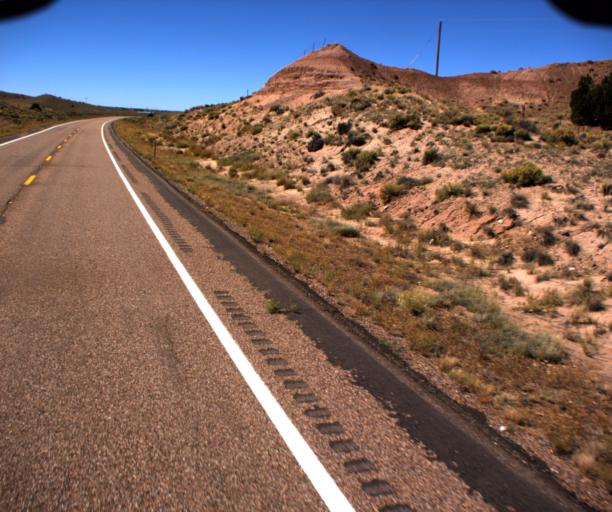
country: US
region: Arizona
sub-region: Apache County
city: Saint Johns
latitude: 34.5852
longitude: -109.5655
